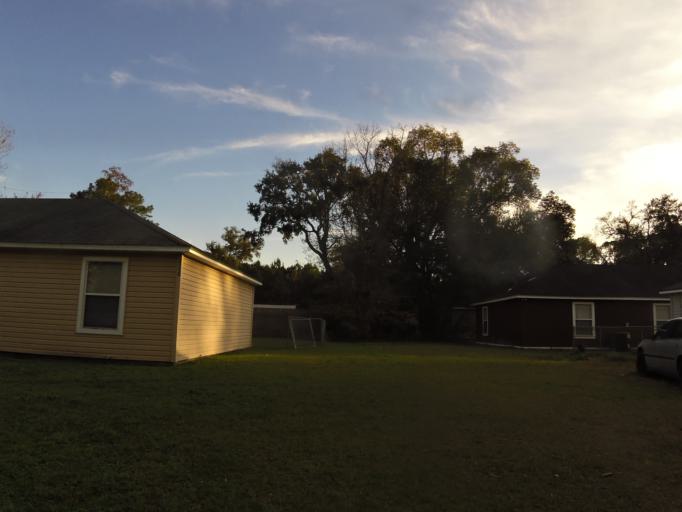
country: US
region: Florida
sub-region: Duval County
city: Jacksonville
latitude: 30.2883
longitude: -81.6417
